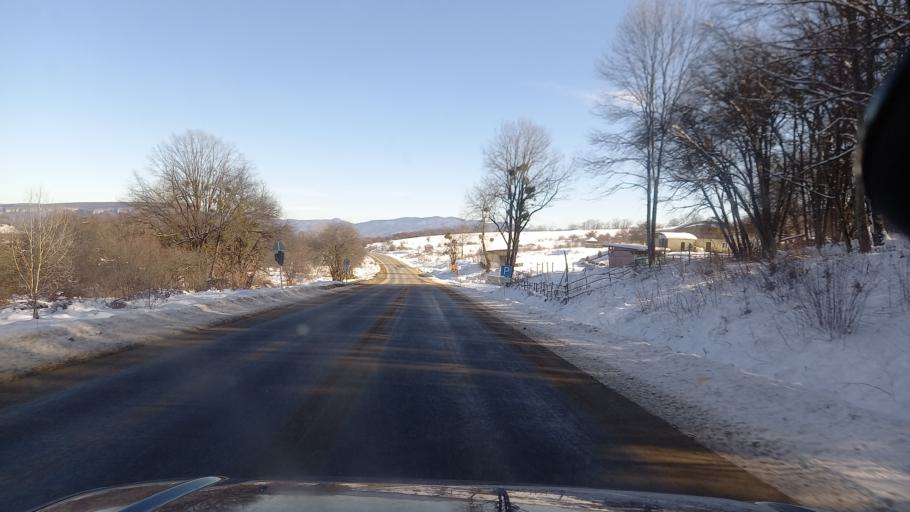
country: RU
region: Adygeya
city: Kamennomostskiy
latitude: 44.2317
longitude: 40.1258
